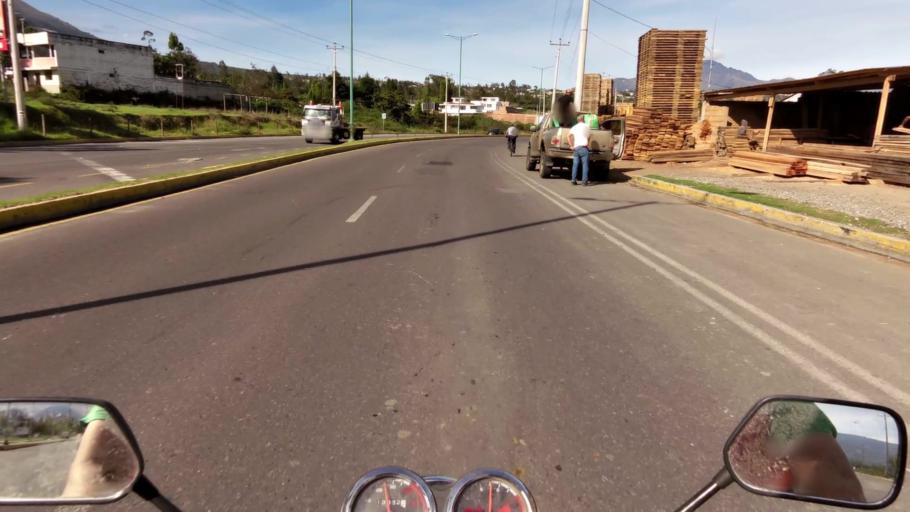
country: EC
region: Imbabura
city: Ibarra
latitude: 0.3312
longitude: -78.1513
